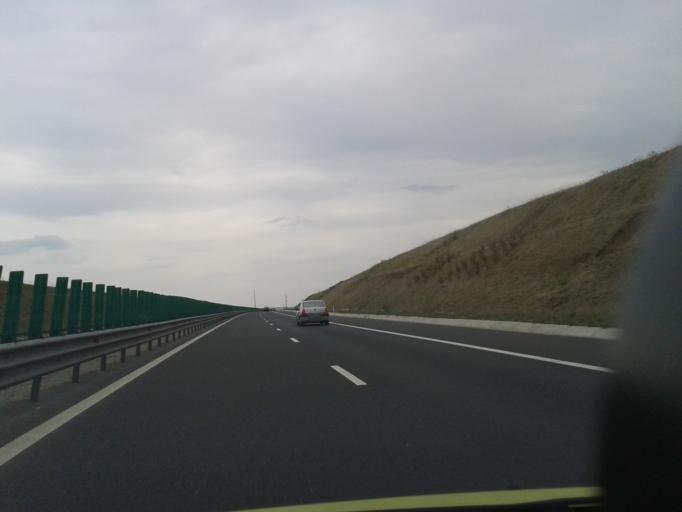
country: RO
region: Alba
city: Vurpar
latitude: 45.9576
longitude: 23.4413
